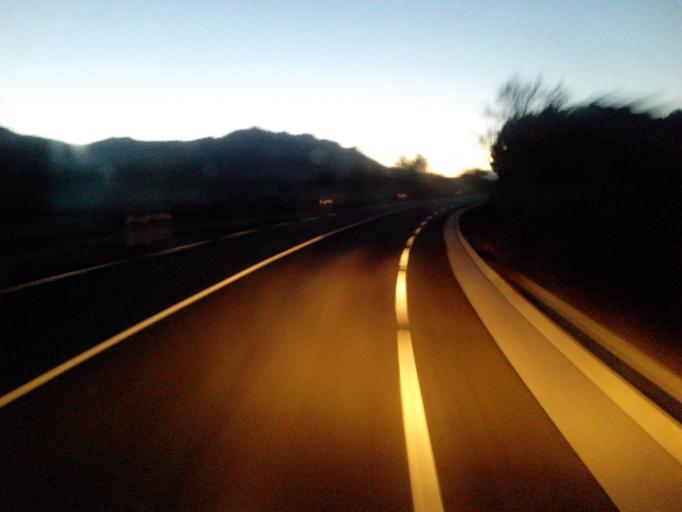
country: FR
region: Languedoc-Roussillon
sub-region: Departement des Pyrenees-Orientales
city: Saint-Paul-de-Fenouillet
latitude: 42.8101
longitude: 2.5779
